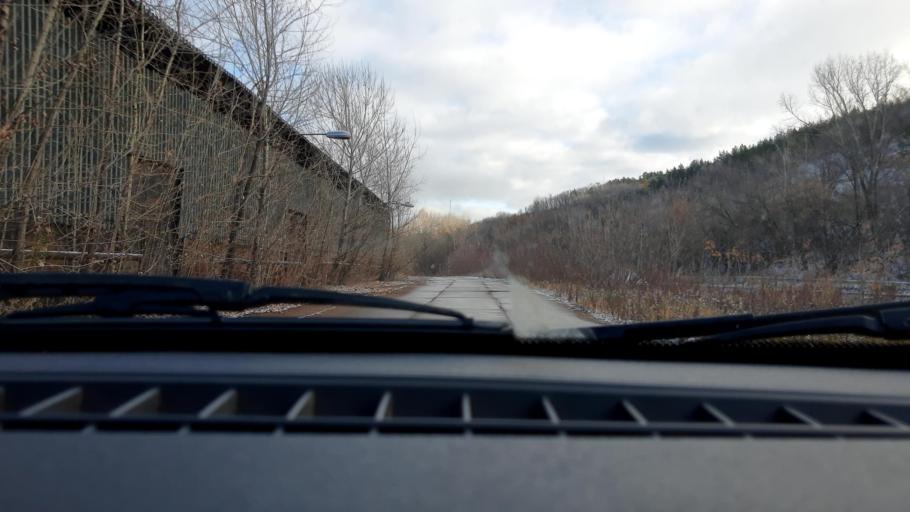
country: RU
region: Bashkortostan
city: Ufa
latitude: 54.7573
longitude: 55.9708
